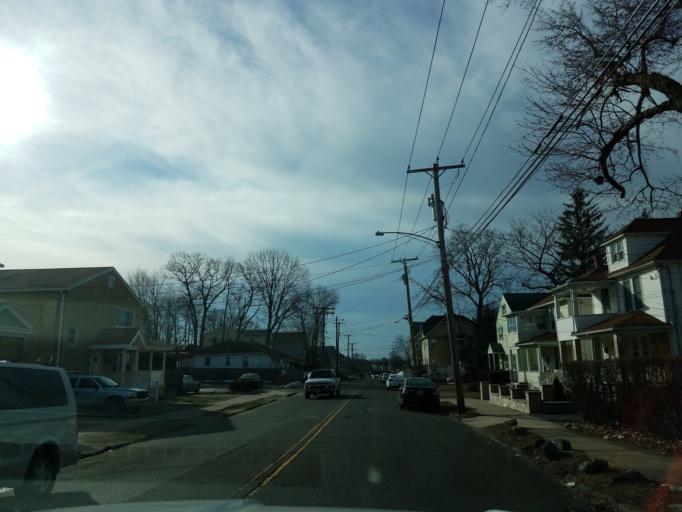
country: US
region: Connecticut
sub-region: Fairfield County
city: Bridgeport
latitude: 41.2036
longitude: -73.2008
